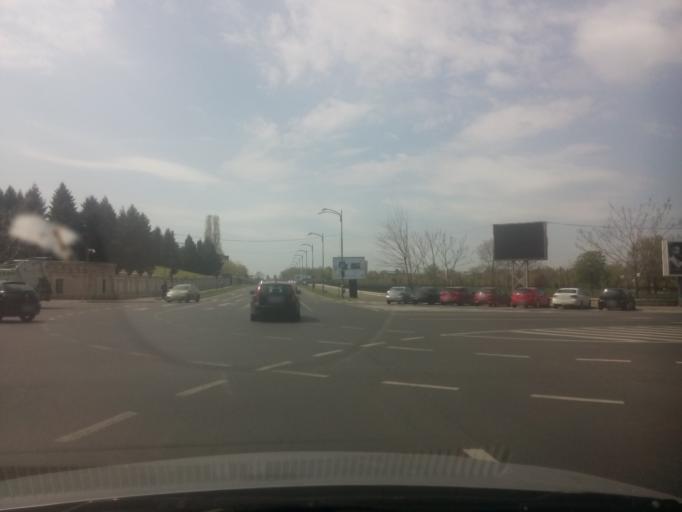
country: RO
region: Bucuresti
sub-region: Municipiul Bucuresti
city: Bucuresti
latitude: 44.4301
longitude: 26.0913
